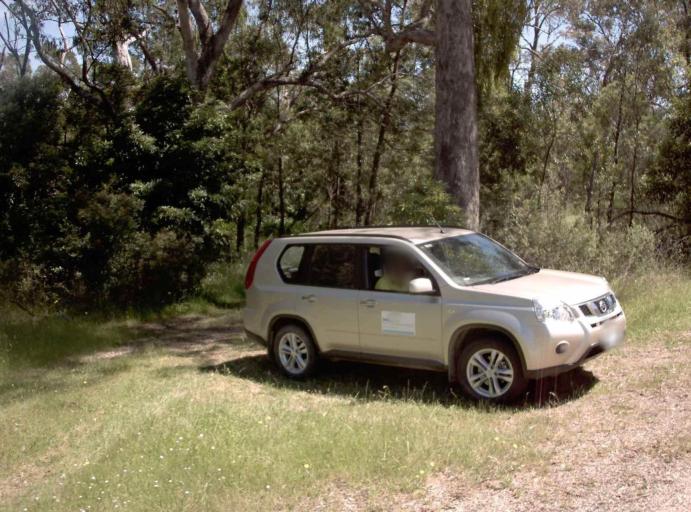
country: AU
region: Victoria
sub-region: East Gippsland
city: Lakes Entrance
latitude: -37.3327
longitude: 148.2332
